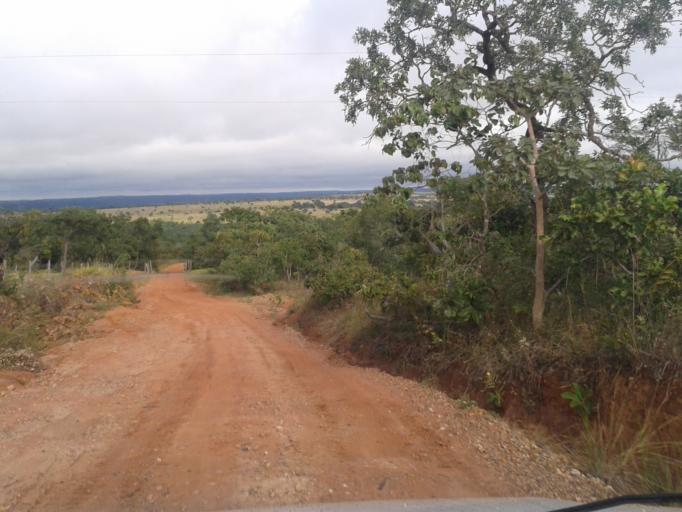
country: BR
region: Minas Gerais
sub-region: Campina Verde
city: Campina Verde
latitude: -19.4030
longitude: -49.6304
